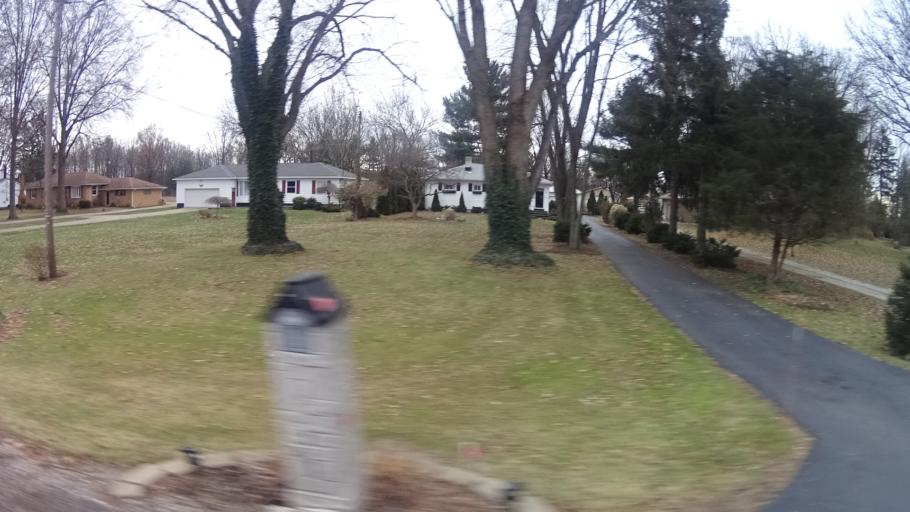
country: US
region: Ohio
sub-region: Lorain County
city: North Ridgeville
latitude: 41.3547
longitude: -82.0313
